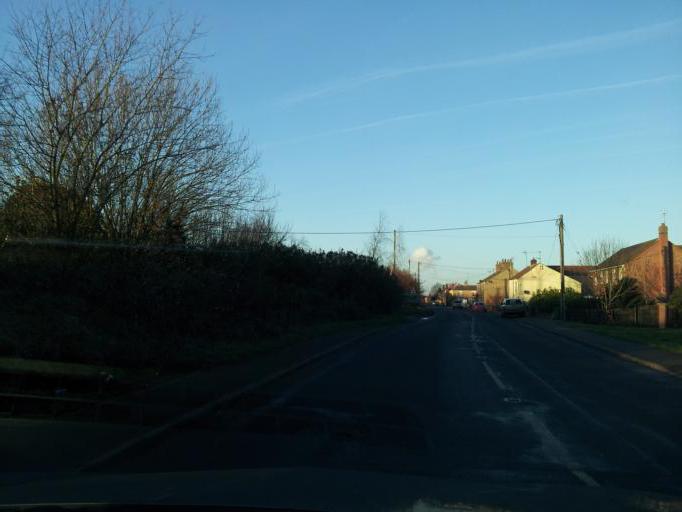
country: GB
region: England
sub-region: Norfolk
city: Outwell
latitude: 52.6113
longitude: 0.2336
